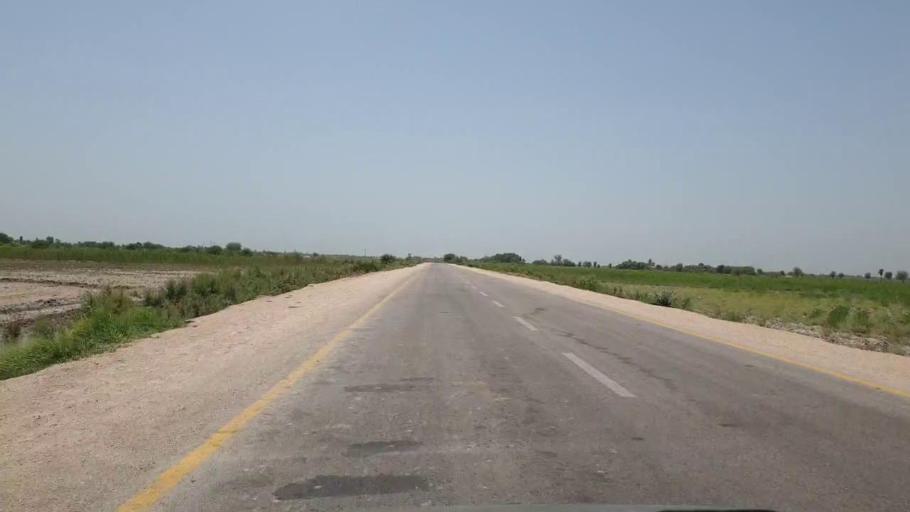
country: PK
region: Sindh
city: Sakrand
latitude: 26.1342
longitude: 68.3743
